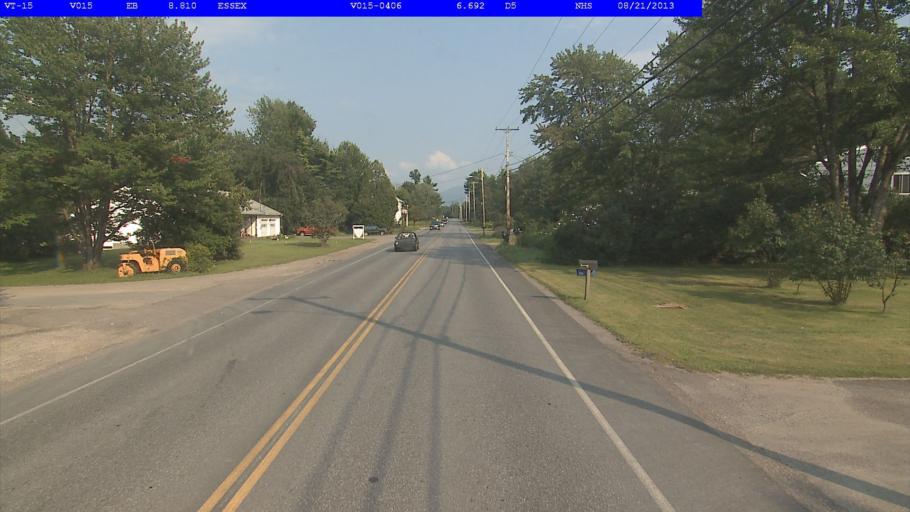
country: US
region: Vermont
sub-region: Chittenden County
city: Jericho
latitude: 44.5037
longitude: -73.0355
